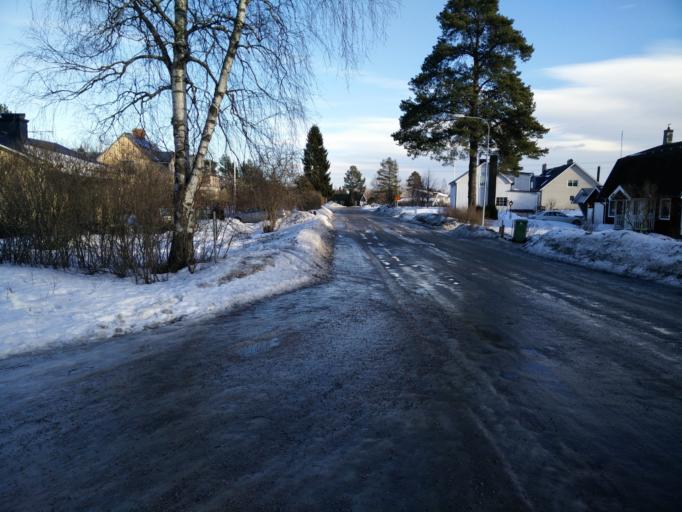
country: SE
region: Vaesternorrland
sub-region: Sundsvalls Kommun
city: Nolby
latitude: 62.2693
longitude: 17.3529
